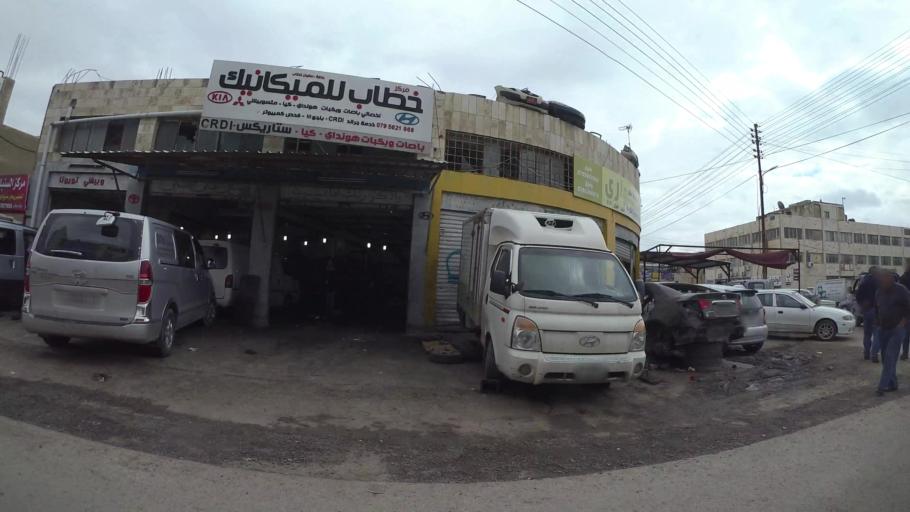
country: JO
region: Amman
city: Wadi as Sir
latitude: 31.9440
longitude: 35.8415
